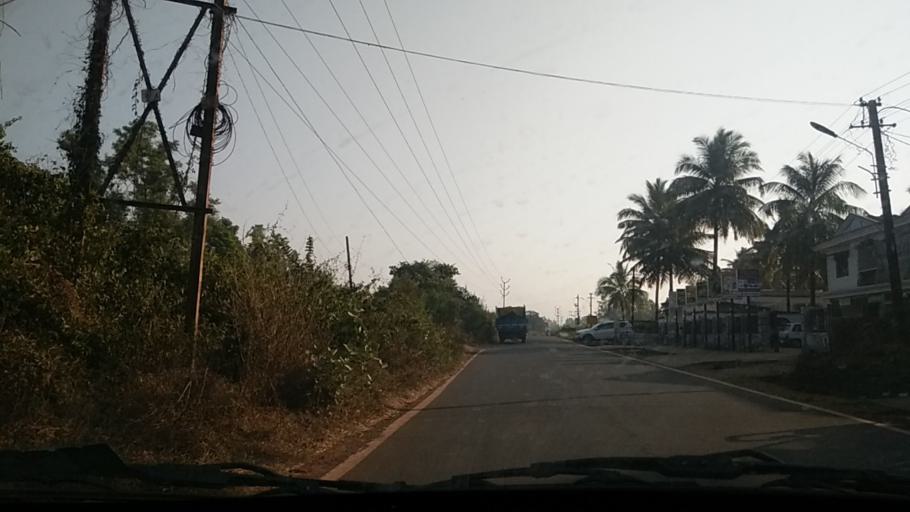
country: IN
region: Goa
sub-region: South Goa
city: Cuncolim
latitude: 15.1876
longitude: 74.0253
